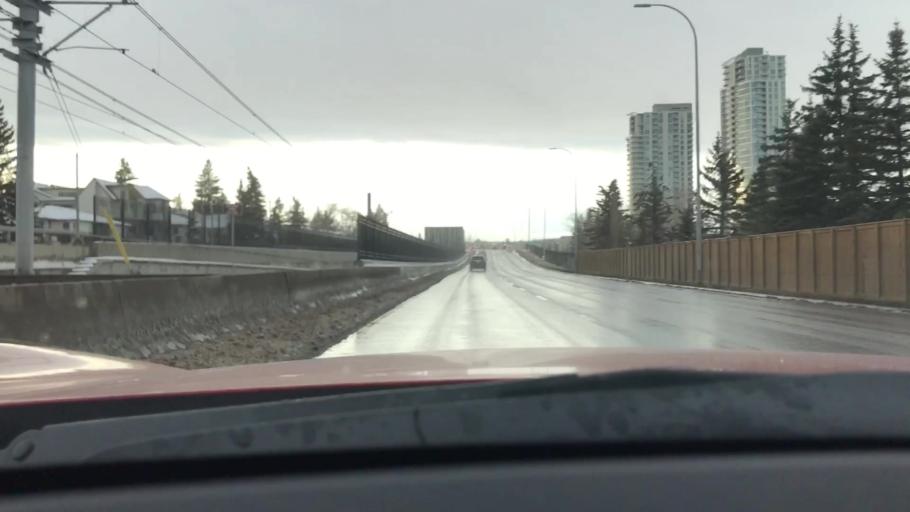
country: CA
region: Alberta
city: Calgary
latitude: 51.0417
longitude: -114.1297
